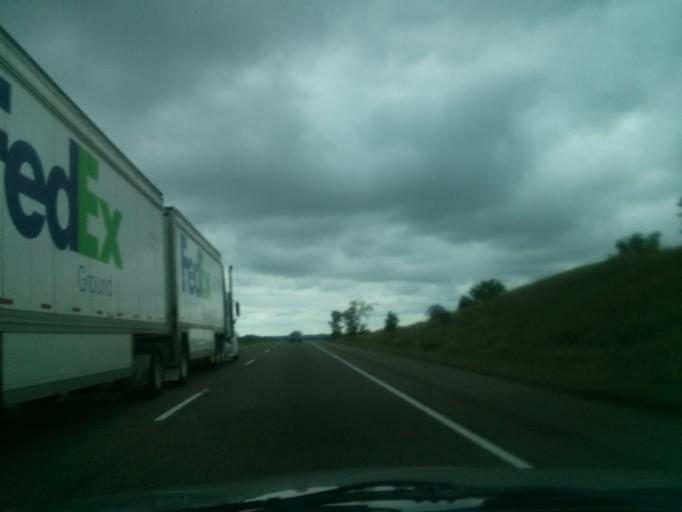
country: US
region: Wisconsin
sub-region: Saint Croix County
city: Hammond
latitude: 44.9418
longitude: -92.4906
